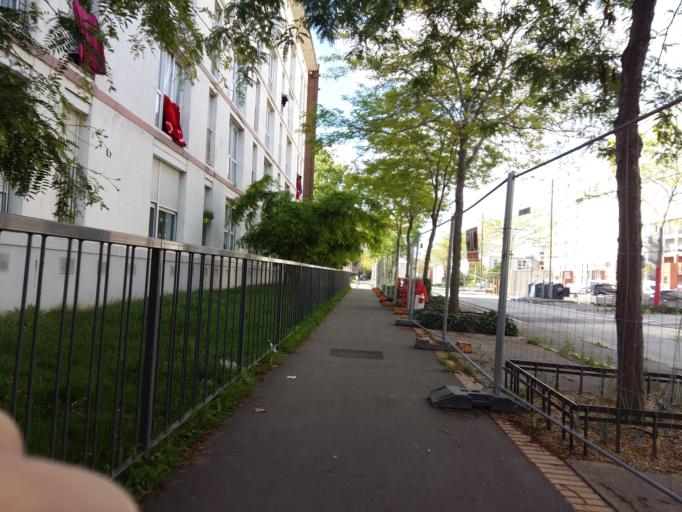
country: FR
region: Picardie
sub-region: Departement de la Somme
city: Amiens
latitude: 49.9133
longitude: 2.3046
